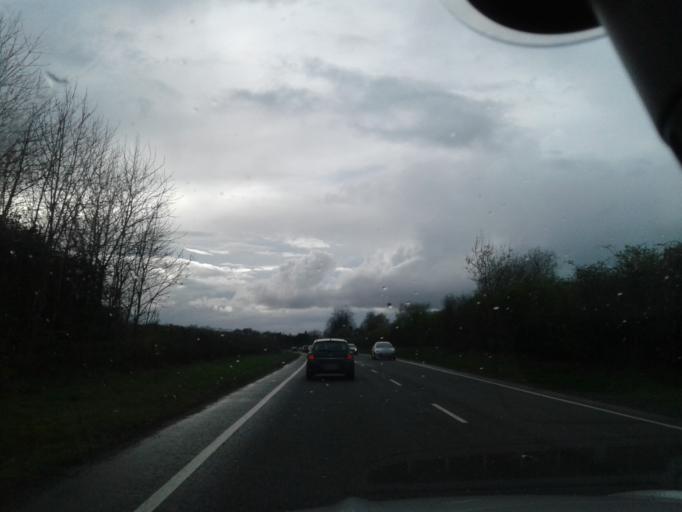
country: GB
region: Northern Ireland
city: Newtownstewart
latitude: 54.7231
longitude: -7.3806
